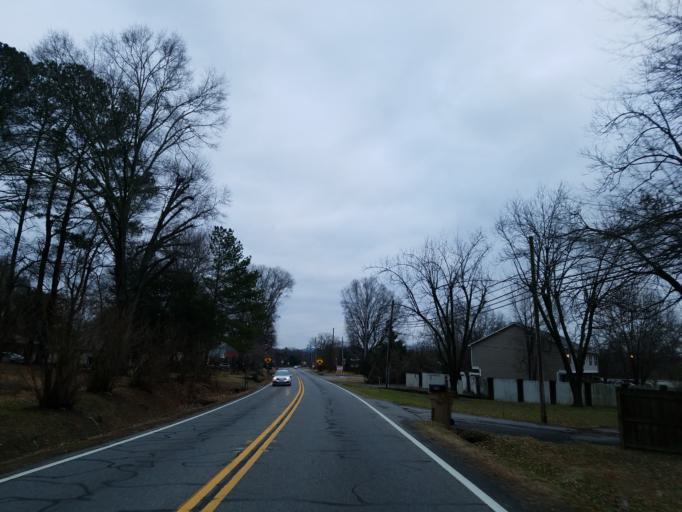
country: US
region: Georgia
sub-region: Bartow County
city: Cartersville
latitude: 34.1920
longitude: -84.8216
